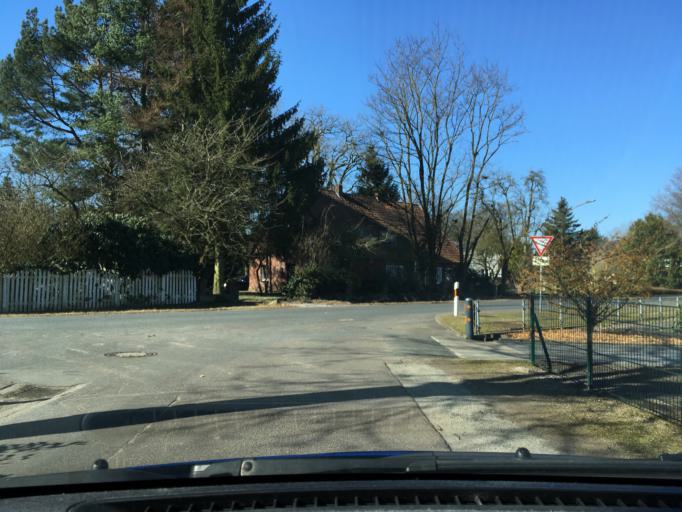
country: DE
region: Lower Saxony
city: Schneverdingen
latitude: 53.0832
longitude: 9.7673
